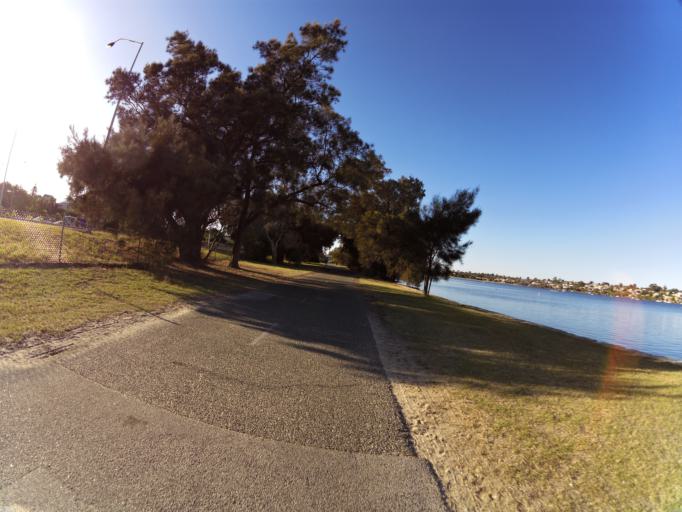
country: AU
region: Western Australia
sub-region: South Perth
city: Manning
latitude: -32.0141
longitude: 115.8570
